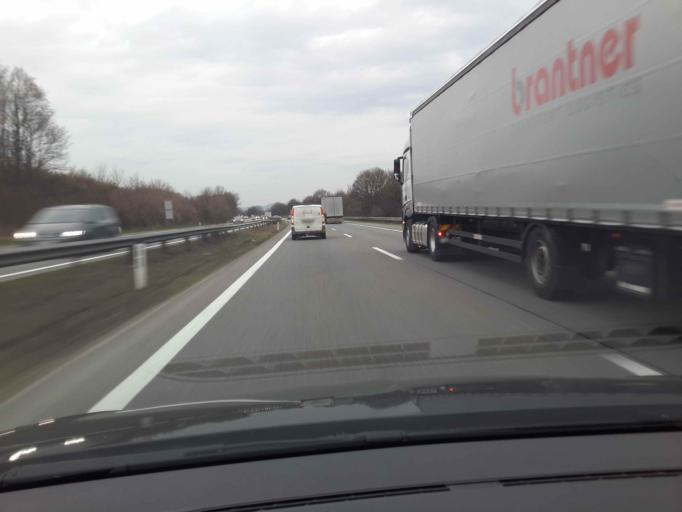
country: AT
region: Lower Austria
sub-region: Politischer Bezirk Melk
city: Klein-Poechlarn
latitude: 48.1980
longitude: 15.2393
